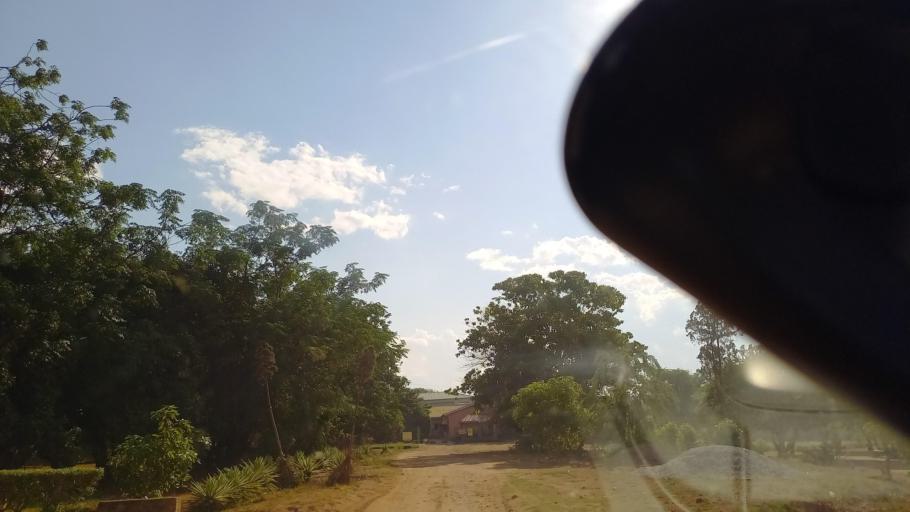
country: ZM
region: Southern
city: Mazabuka
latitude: -15.8629
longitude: 27.7611
